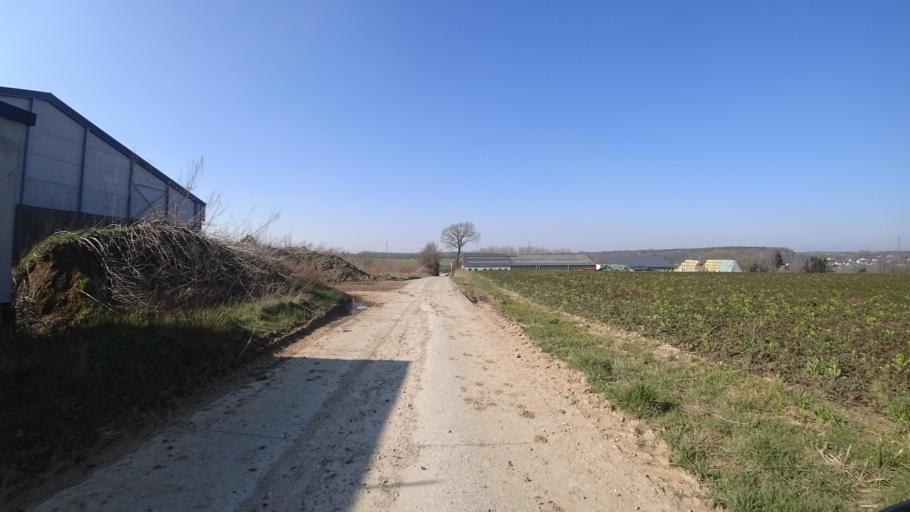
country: BE
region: Wallonia
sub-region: Province du Brabant Wallon
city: Mont-Saint-Guibert
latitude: 50.6331
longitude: 4.5963
